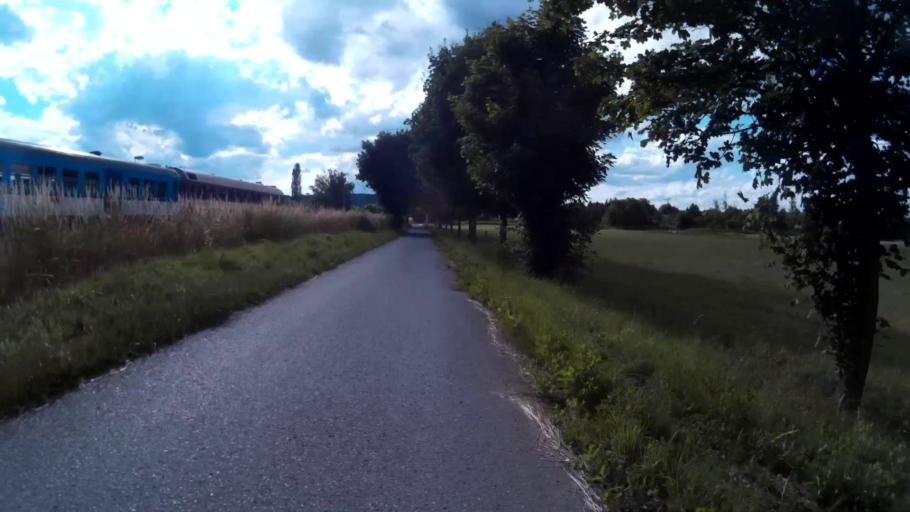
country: CZ
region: South Moravian
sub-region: Okres Brno-Venkov
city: Rosice
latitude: 49.1725
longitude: 16.4083
